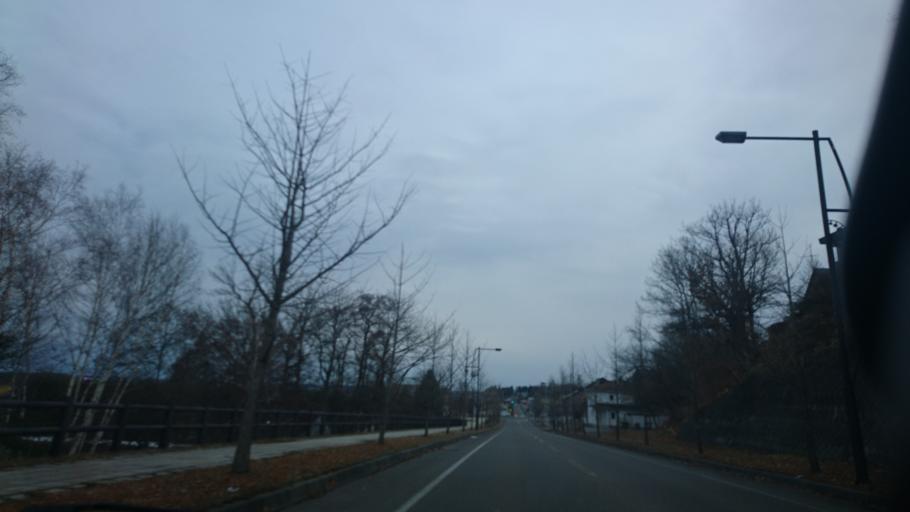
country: JP
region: Hokkaido
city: Otofuke
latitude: 42.9588
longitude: 143.2005
